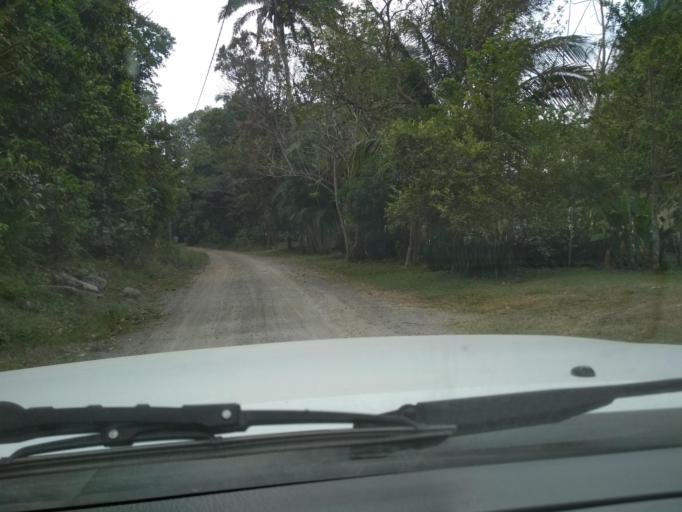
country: MX
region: Veracruz
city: El Tejar
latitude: 19.0745
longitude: -96.1708
